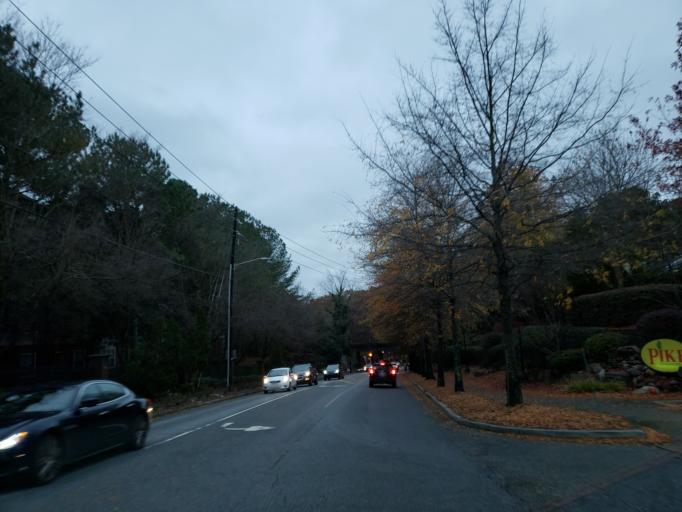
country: US
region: Georgia
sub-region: DeKalb County
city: Druid Hills
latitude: 33.8210
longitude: -84.3714
